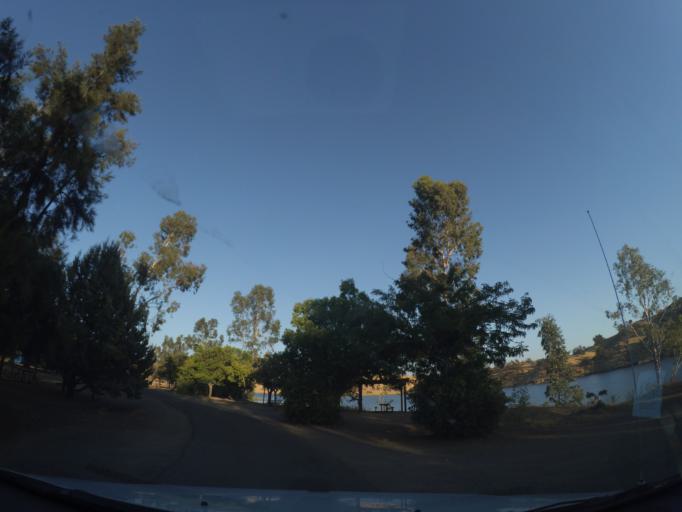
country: US
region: California
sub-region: Merced County
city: Planada
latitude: 37.5198
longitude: -120.3012
